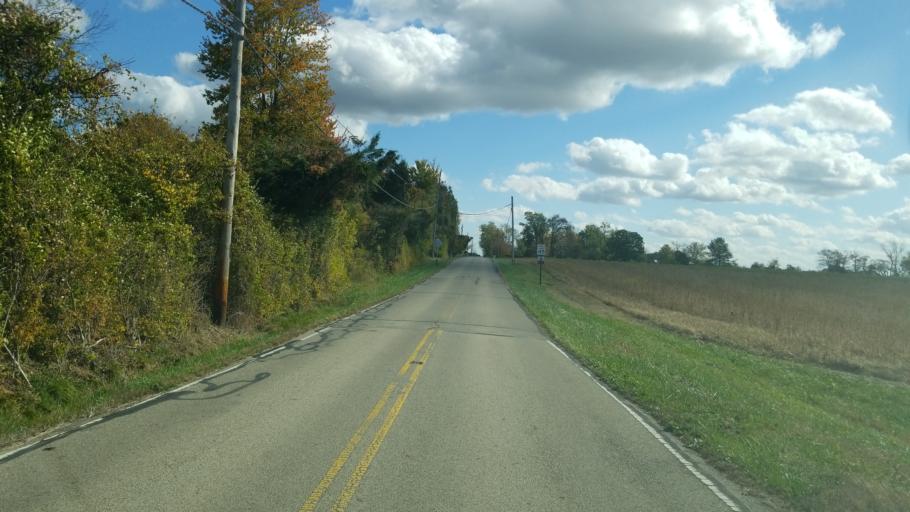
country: US
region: Ohio
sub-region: Warren County
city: South Lebanon
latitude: 39.3876
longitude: -84.1665
